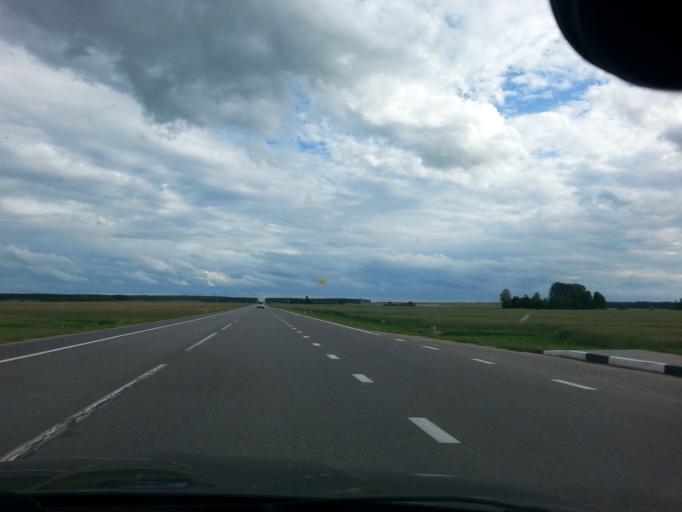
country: BY
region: Grodnenskaya
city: Astravyets
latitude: 54.7326
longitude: 26.0867
